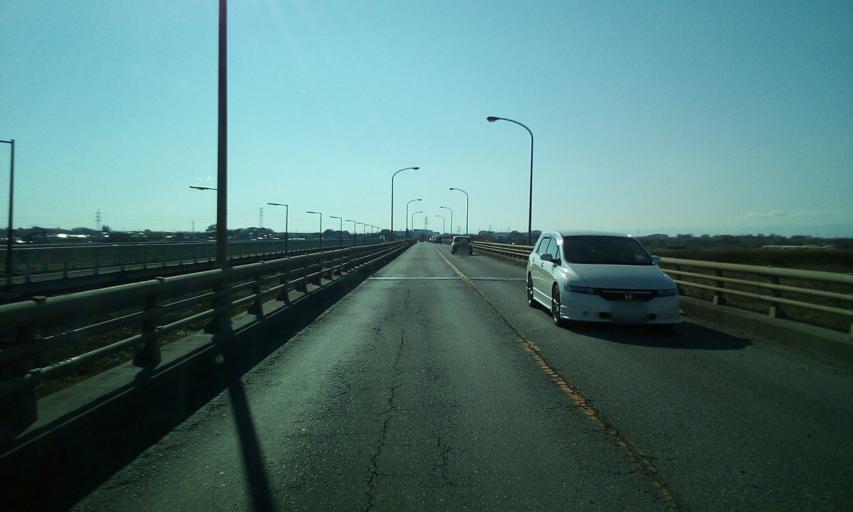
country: JP
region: Ibaraki
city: Sakai
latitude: 36.0991
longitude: 139.7921
